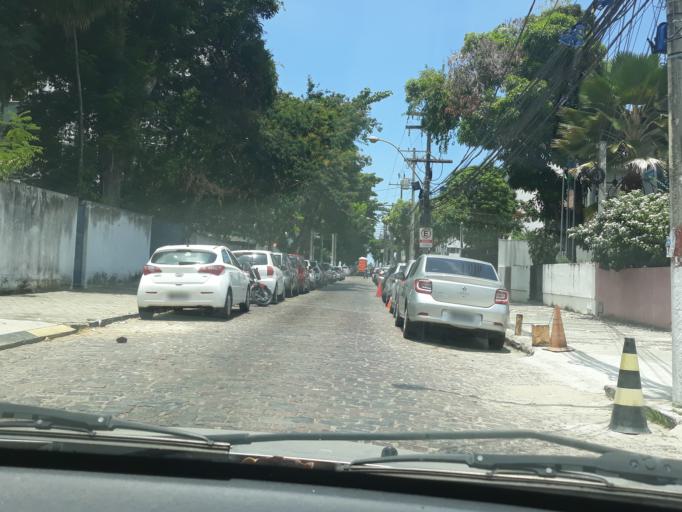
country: BR
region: Bahia
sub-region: Salvador
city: Salvador
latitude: -13.0081
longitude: -38.5082
